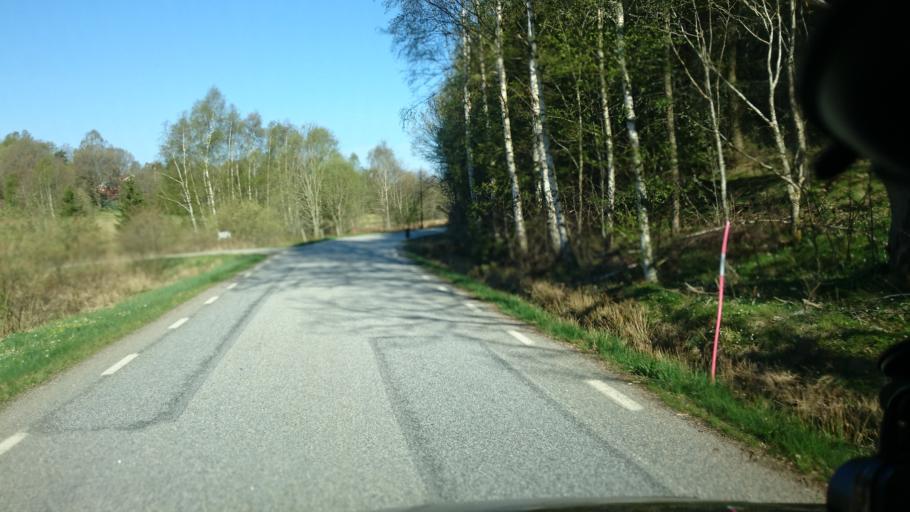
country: SE
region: Vaestra Goetaland
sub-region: Munkedals Kommun
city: Munkedal
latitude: 58.3714
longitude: 11.6898
